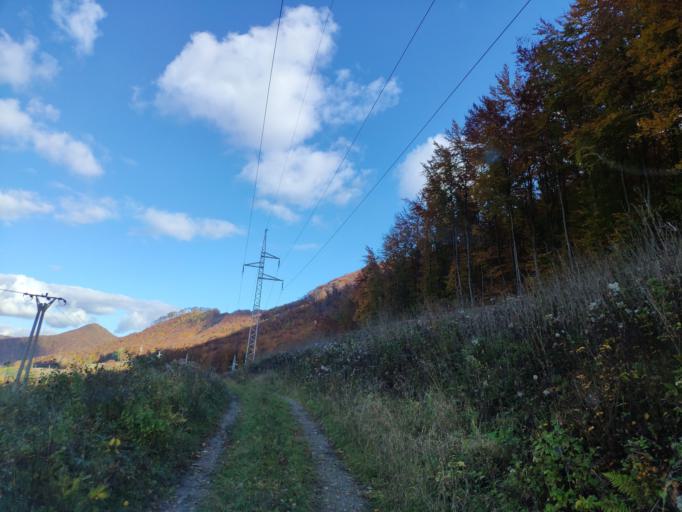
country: SK
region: Presovsky
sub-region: Okres Presov
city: Presov
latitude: 48.8508
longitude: 21.1741
